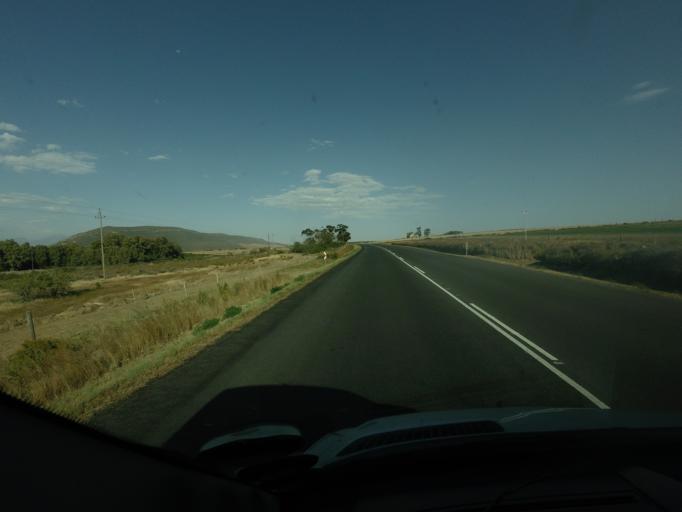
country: ZA
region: Western Cape
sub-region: Cape Winelands District Municipality
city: Ashton
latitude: -34.0925
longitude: 20.1197
